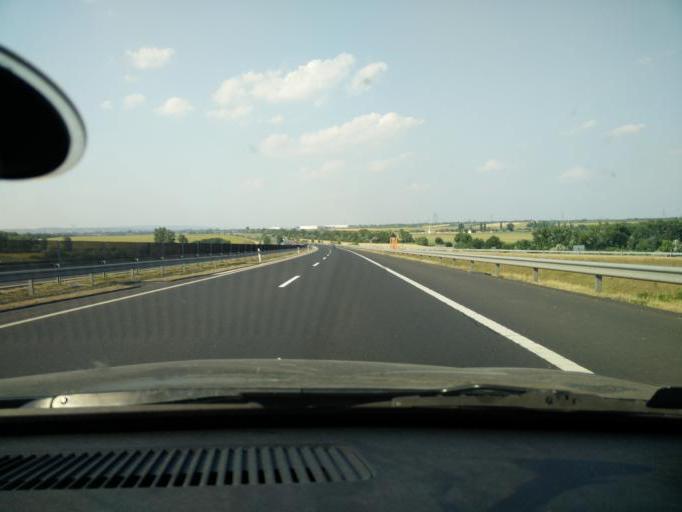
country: HU
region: Pest
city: Szazhalombatta
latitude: 47.3370
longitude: 18.8932
